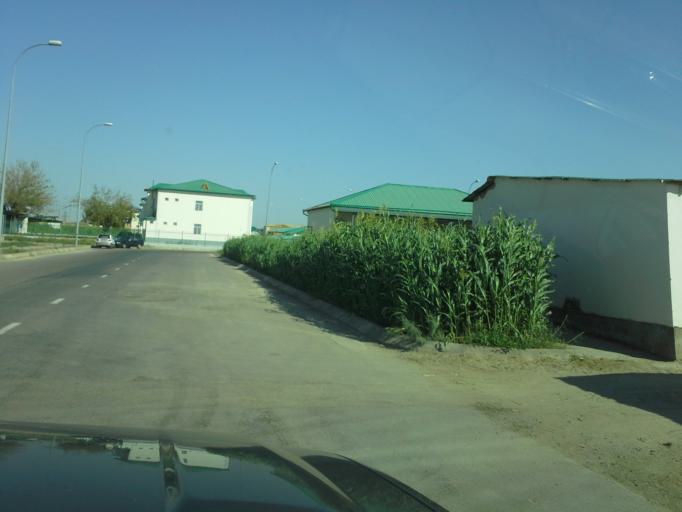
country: TM
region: Dasoguz
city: Dasoguz
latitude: 41.8194
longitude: 59.9552
